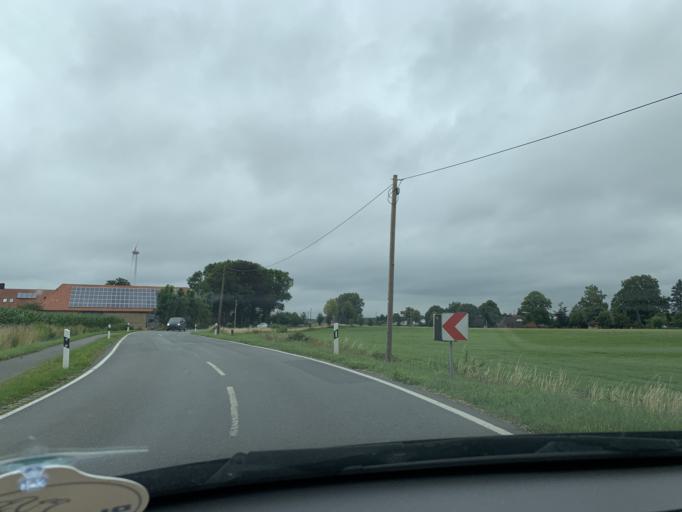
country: DE
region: North Rhine-Westphalia
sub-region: Regierungsbezirk Munster
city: Laer
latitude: 52.1048
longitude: 7.3589
